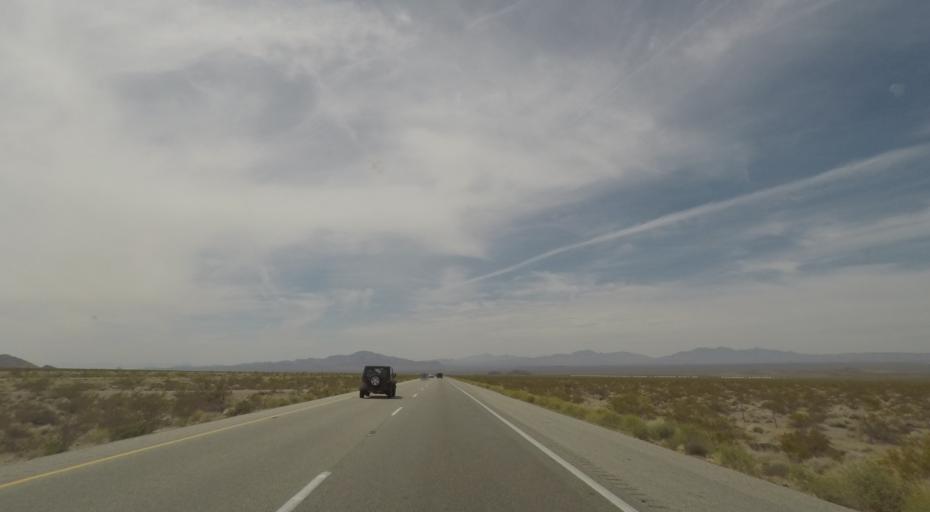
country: US
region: California
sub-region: San Bernardino County
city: Needles
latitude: 34.8218
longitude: -115.1156
